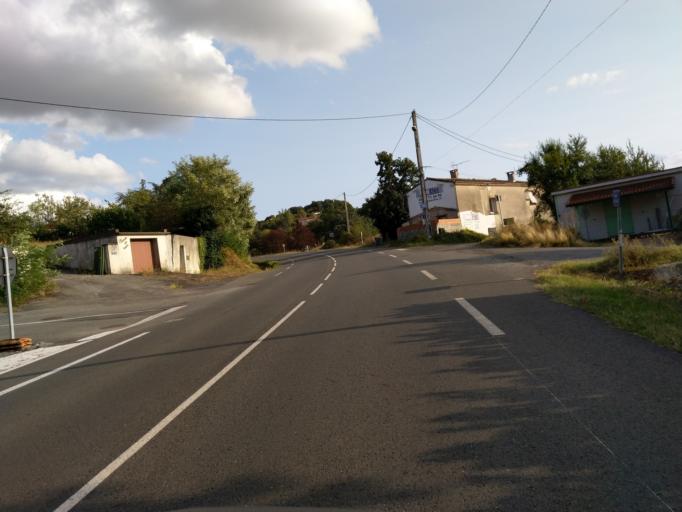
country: FR
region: Midi-Pyrenees
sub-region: Departement du Tarn
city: Puygouzon
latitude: 43.9153
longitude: 2.1895
